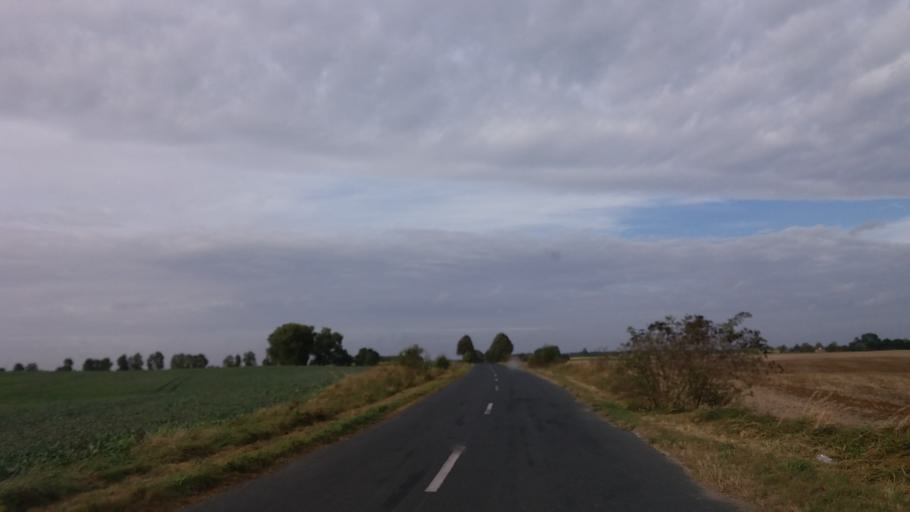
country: PL
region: West Pomeranian Voivodeship
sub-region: Powiat choszczenski
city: Krzecin
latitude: 53.0485
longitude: 15.4920
